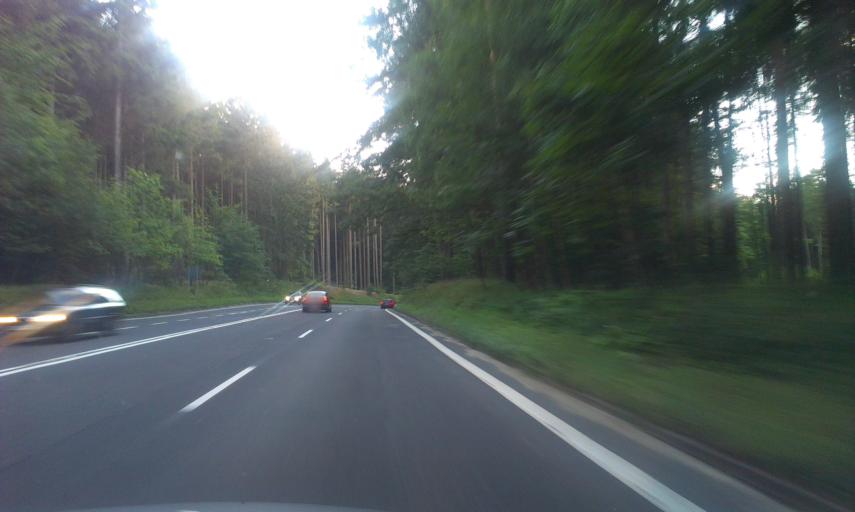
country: PL
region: West Pomeranian Voivodeship
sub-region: Koszalin
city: Koszalin
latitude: 54.2143
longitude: 16.2217
